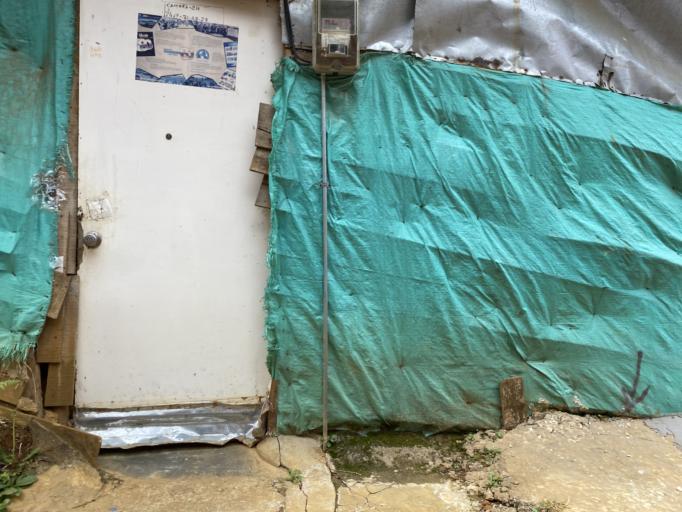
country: CO
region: Antioquia
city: Medellin
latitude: 6.2662
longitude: -75.5392
